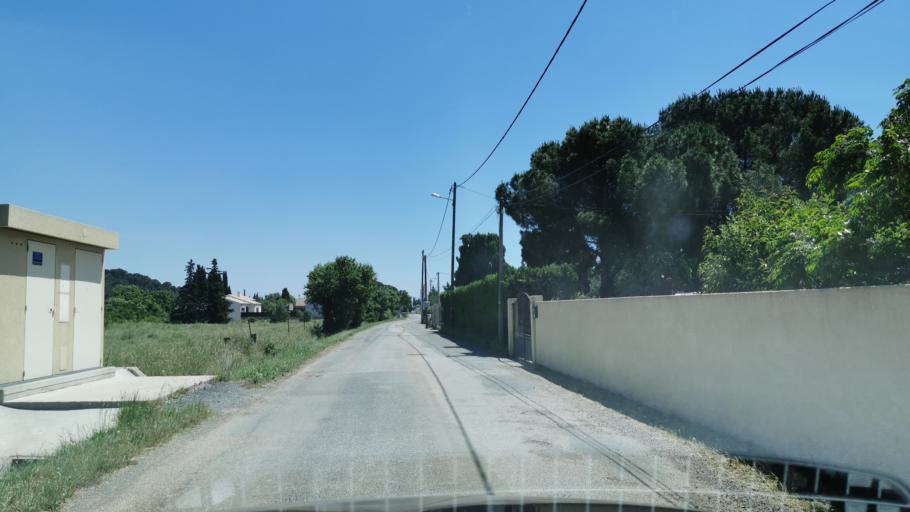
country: FR
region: Languedoc-Roussillon
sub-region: Departement de l'Aude
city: Saint-Marcel-sur-Aude
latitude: 43.2651
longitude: 2.9488
